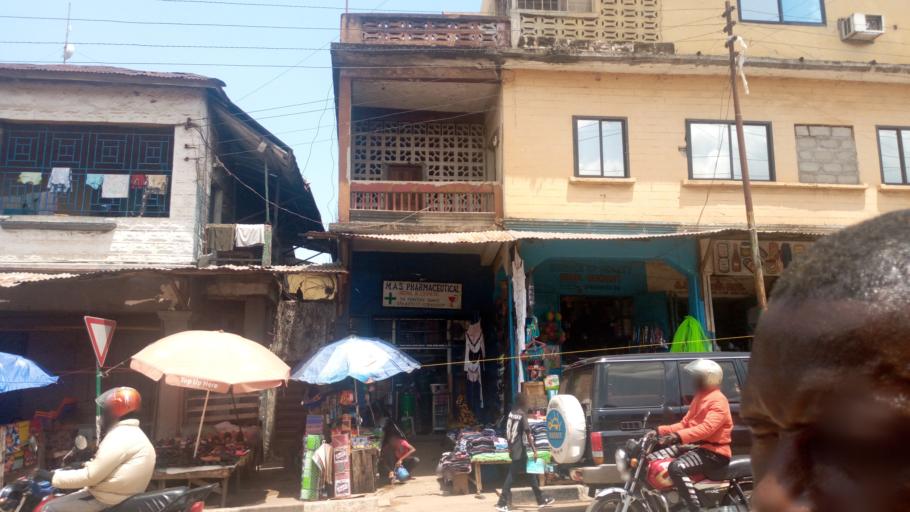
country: SL
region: Southern Province
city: Bo
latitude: 7.9648
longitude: -11.7382
